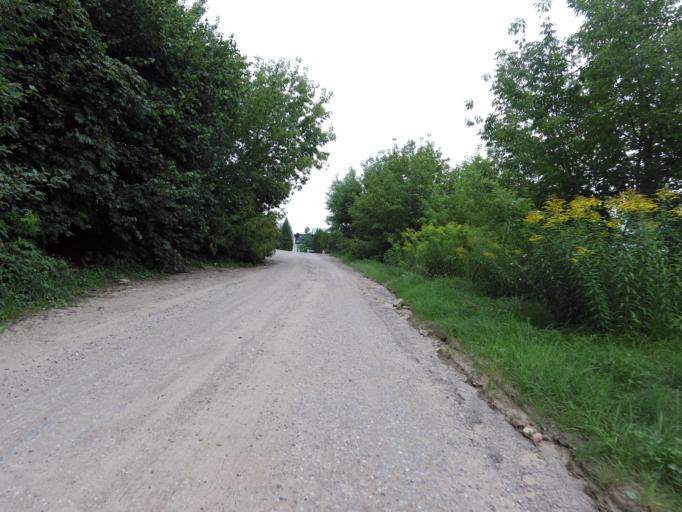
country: LT
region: Vilnius County
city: Seskine
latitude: 54.7224
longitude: 25.2783
